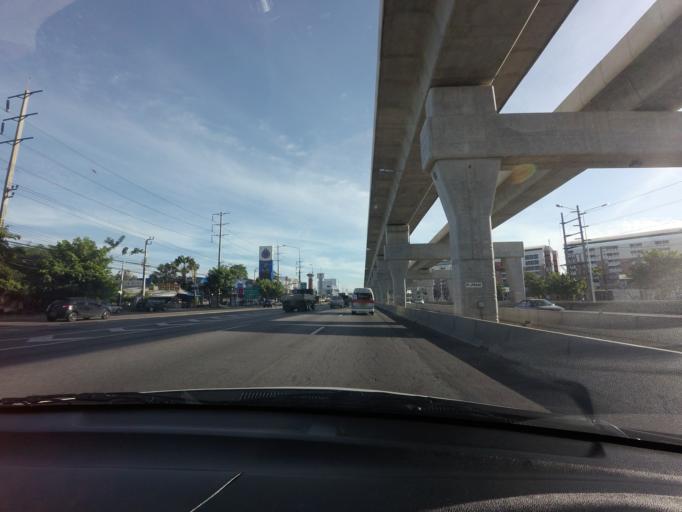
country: TH
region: Nonthaburi
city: Bang Bua Thong
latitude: 13.8862
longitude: 100.4087
